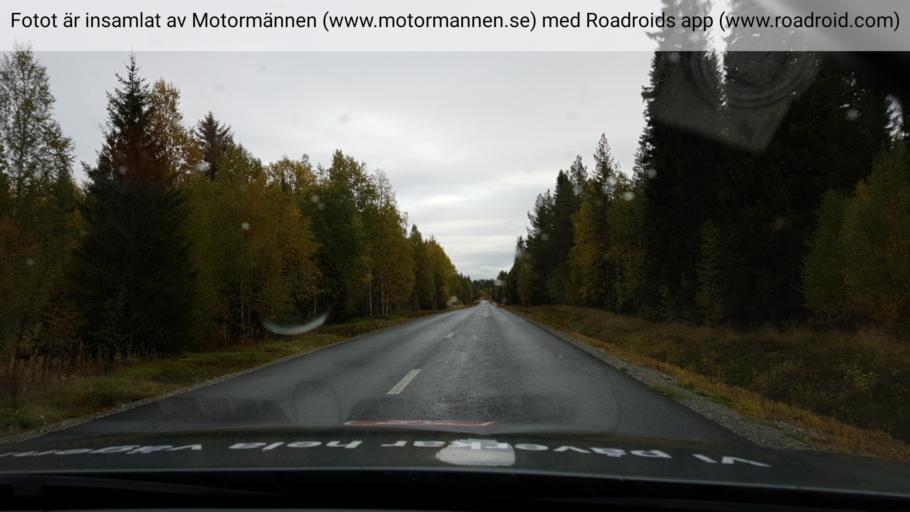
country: SE
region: Vaesterbotten
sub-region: Vilhelmina Kommun
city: Sjoberg
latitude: 64.7089
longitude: 16.2487
